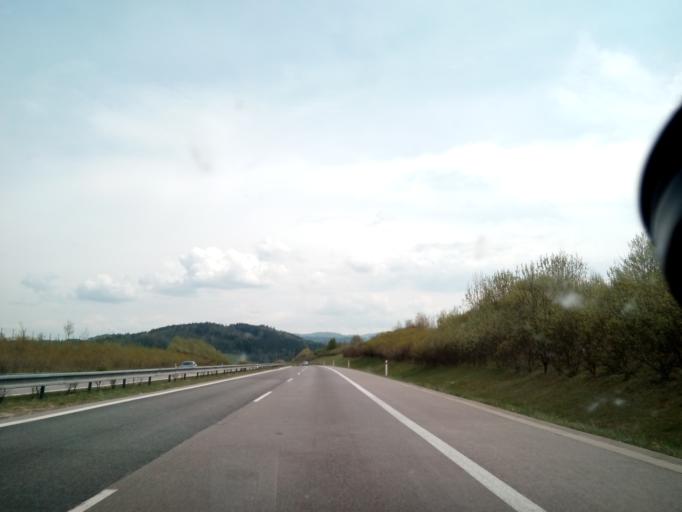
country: SK
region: Trenciansky
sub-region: Okres Povazska Bystrica
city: Povazska Bystrica
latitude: 49.0631
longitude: 18.3717
